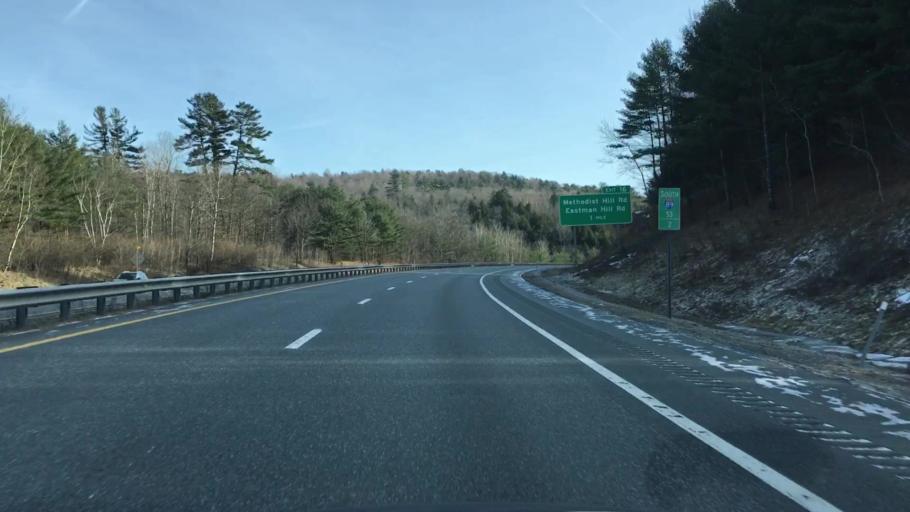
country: US
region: New Hampshire
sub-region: Grafton County
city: Lebanon
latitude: 43.6248
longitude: -72.2023
